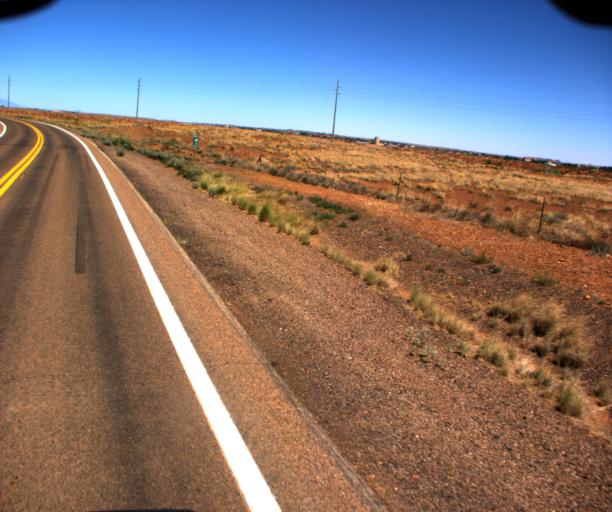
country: US
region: Arizona
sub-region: Navajo County
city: Winslow
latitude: 35.0055
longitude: -110.6919
